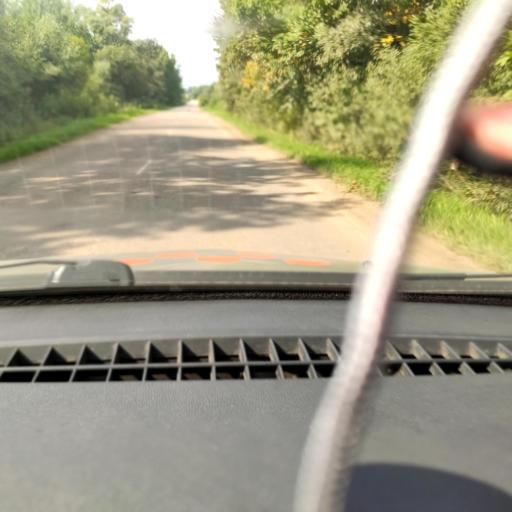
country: RU
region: Bashkortostan
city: Kudeyevskiy
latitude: 54.7340
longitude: 56.6077
